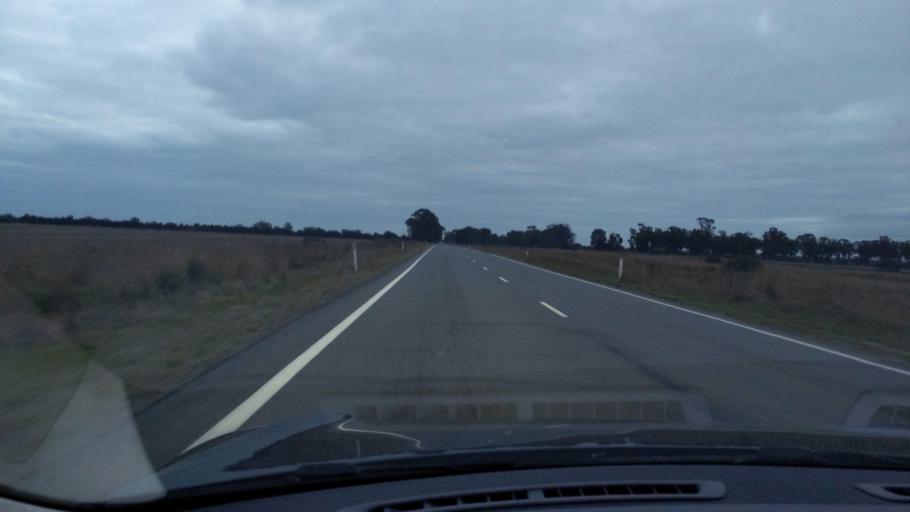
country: AU
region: New South Wales
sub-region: Narrandera
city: Narrandera
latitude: -34.7580
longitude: 146.8719
